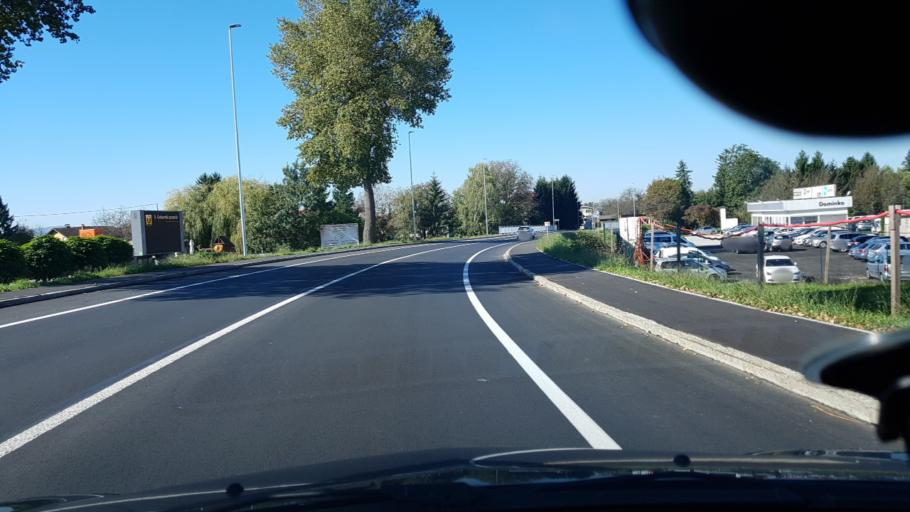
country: SI
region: Ptuj
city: Ptuj
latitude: 46.4152
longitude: 15.8673
